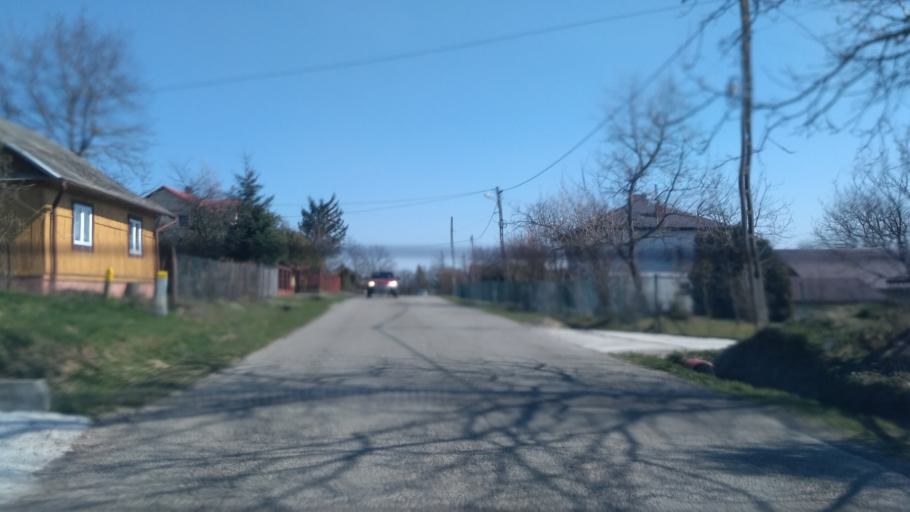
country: PL
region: Subcarpathian Voivodeship
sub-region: Powiat jaroslawski
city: Jodlowka
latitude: 49.9279
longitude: 22.4807
